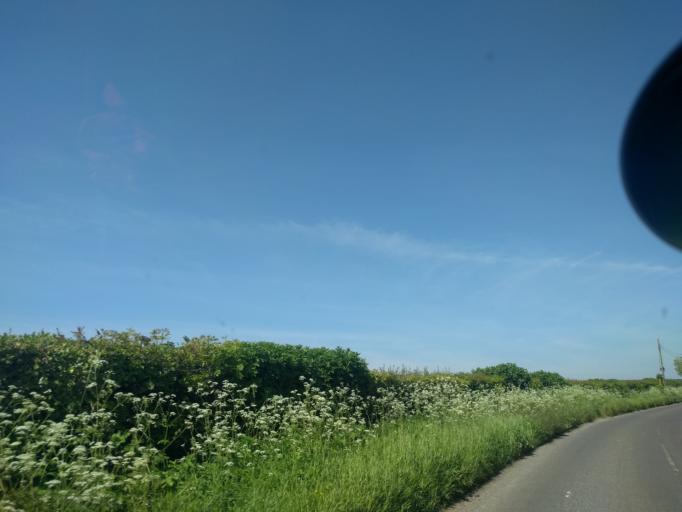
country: GB
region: England
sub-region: Somerset
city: Langport
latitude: 51.0570
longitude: -2.8168
